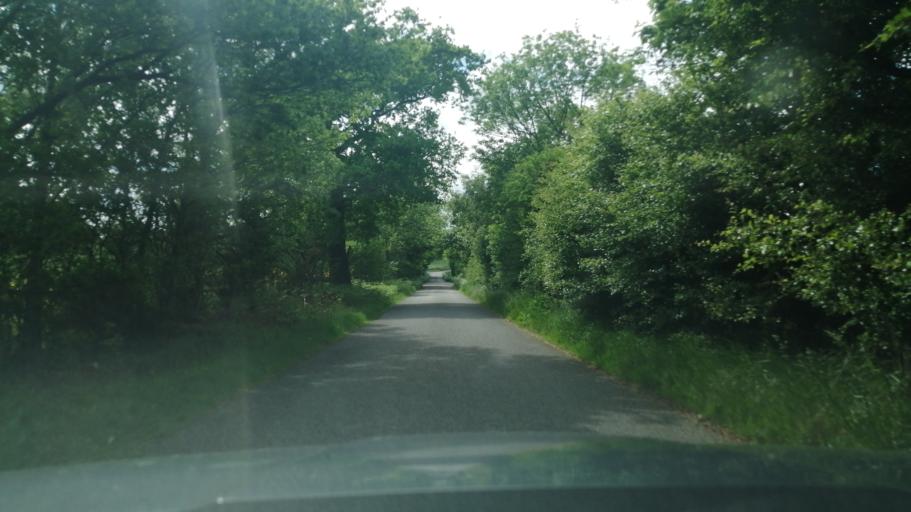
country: GB
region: Scotland
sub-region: Moray
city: Elgin
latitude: 57.6541
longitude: -3.2725
